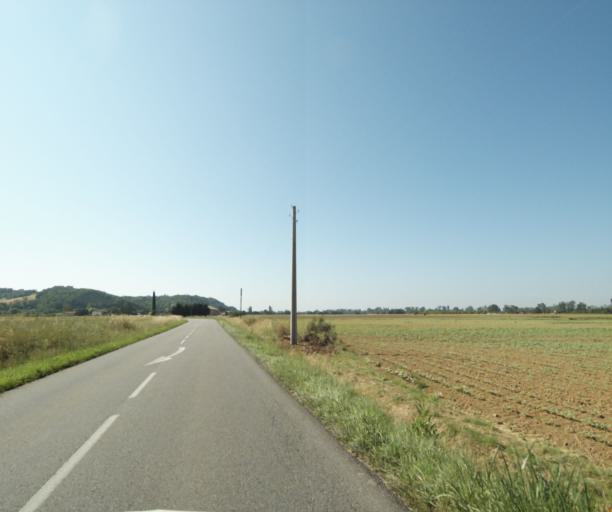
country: FR
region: Midi-Pyrenees
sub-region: Departement du Tarn-et-Garonne
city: Bressols
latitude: 43.9649
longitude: 1.3584
